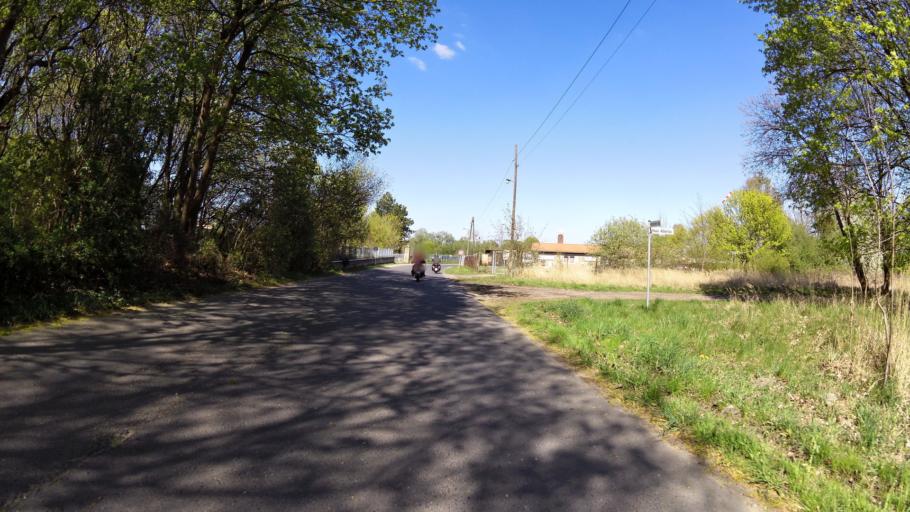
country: DE
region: Brandenburg
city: Muncheberg
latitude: 52.5082
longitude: 14.1378
